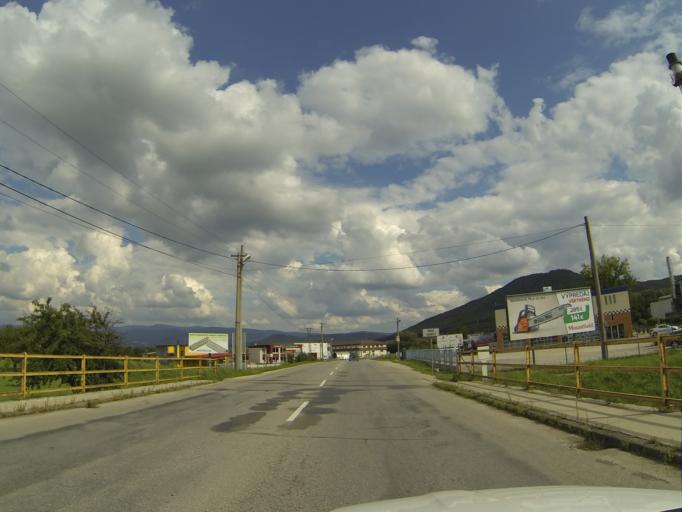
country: SK
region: Nitriansky
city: Partizanske
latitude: 48.6271
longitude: 18.3969
